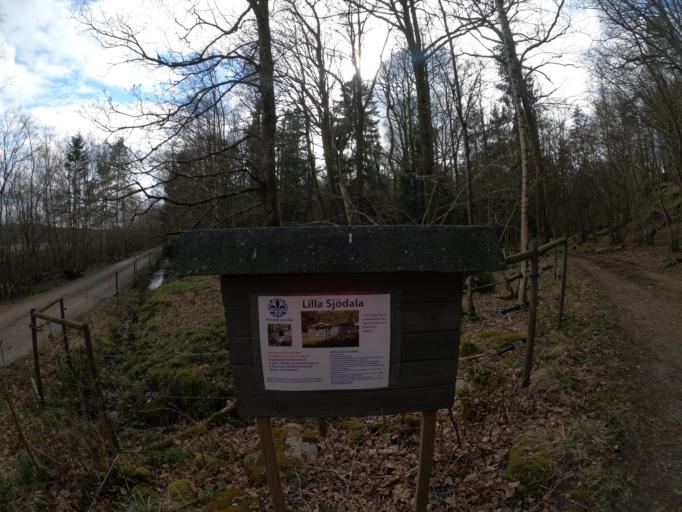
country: SE
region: Vaestra Goetaland
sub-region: Harryda Kommun
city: Molnlycke
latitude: 57.6315
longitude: 12.0964
